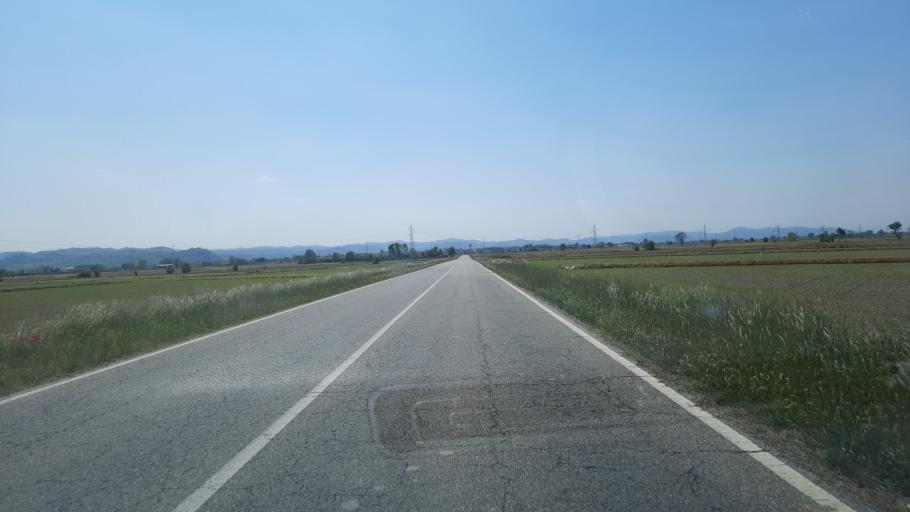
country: IT
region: Piedmont
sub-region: Provincia di Vercelli
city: Lamporo
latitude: 45.2106
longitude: 8.1257
